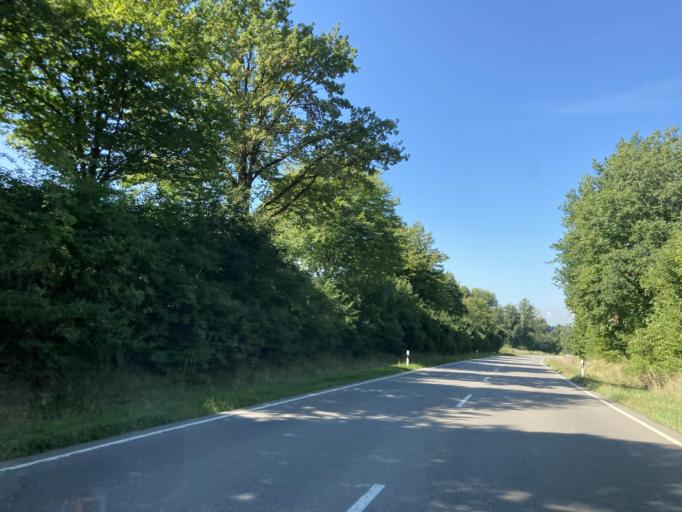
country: DE
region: Baden-Wuerttemberg
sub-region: Tuebingen Region
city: Durmentingen
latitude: 48.1381
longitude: 9.5497
